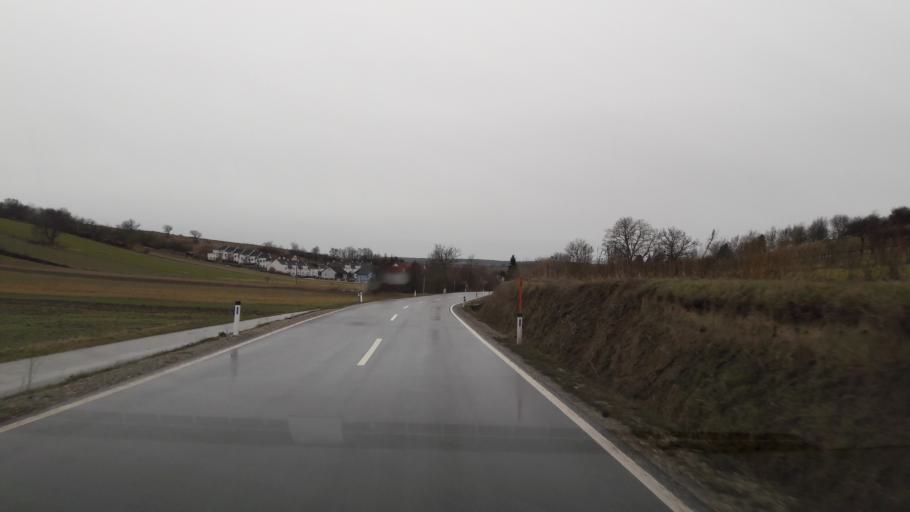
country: AT
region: Lower Austria
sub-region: Politischer Bezirk Mistelbach
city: Hochleithen
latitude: 48.4422
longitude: 16.5355
